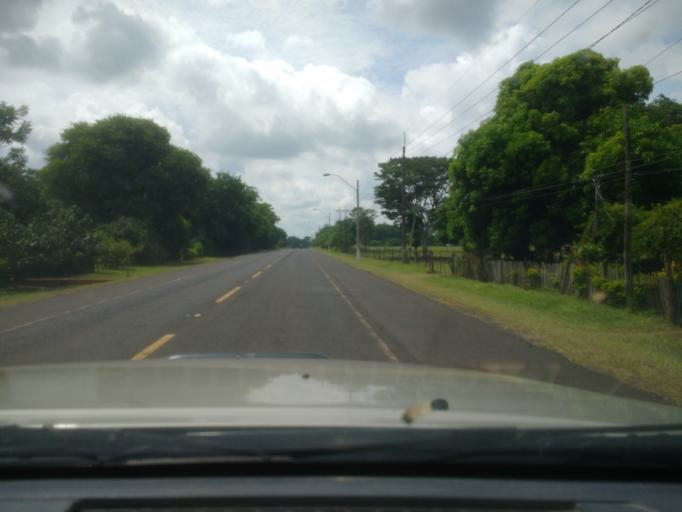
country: PY
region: San Pedro
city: Puerto Rosario
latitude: -24.4218
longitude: -57.0897
